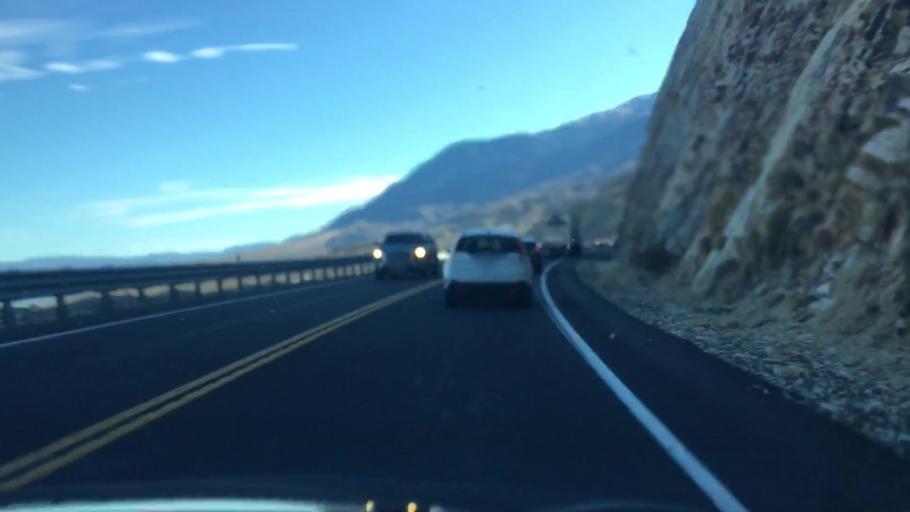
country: US
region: Nevada
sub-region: Mineral County
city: Hawthorne
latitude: 38.6684
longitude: -118.7677
